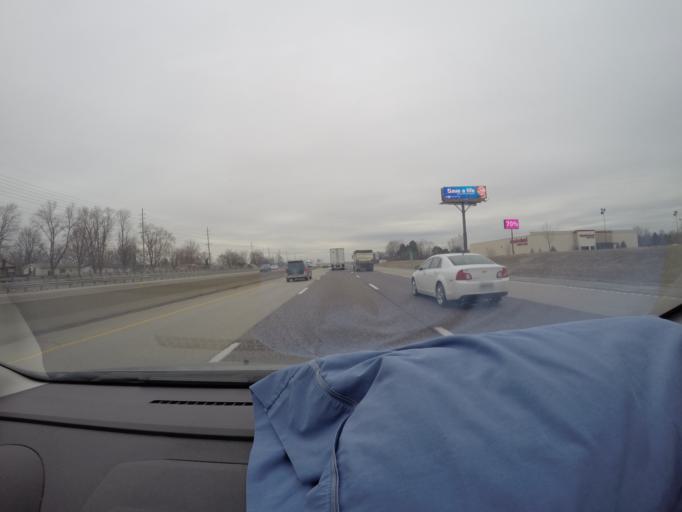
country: US
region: Missouri
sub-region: Saint Charles County
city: O'Fallon
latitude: 38.8027
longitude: -90.6907
